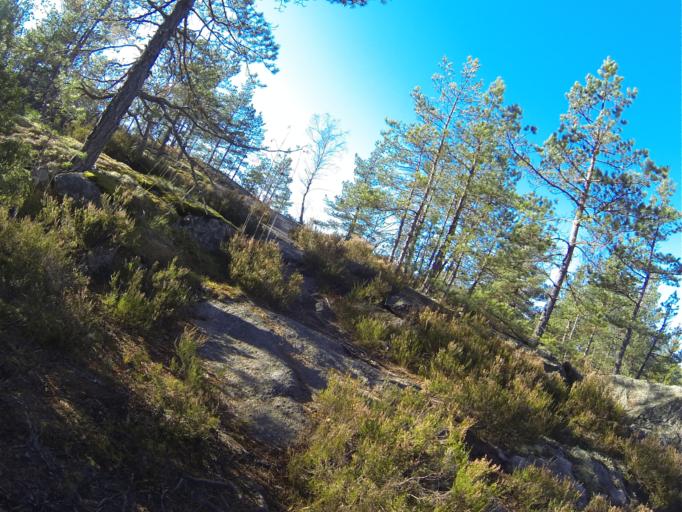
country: FI
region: Varsinais-Suomi
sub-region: Salo
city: Saerkisalo
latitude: 60.2035
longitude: 22.9379
